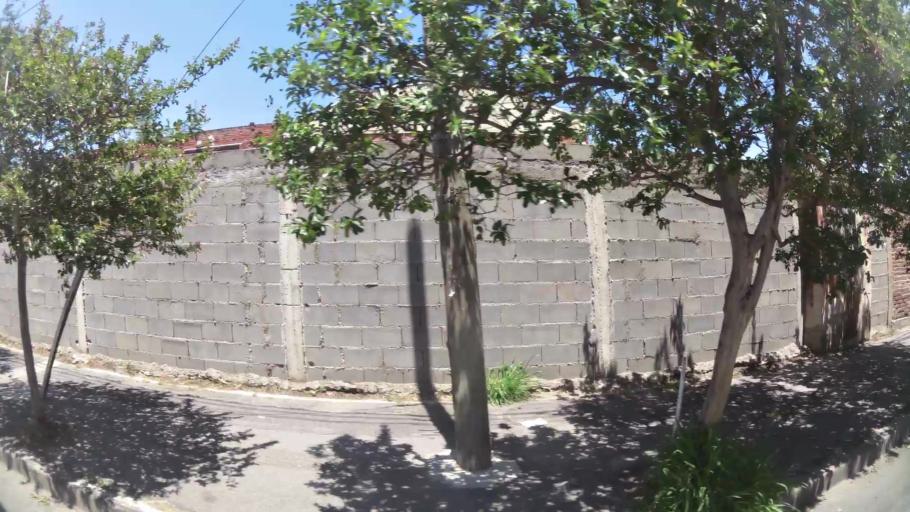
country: AR
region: Cordoba
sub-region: Departamento de Capital
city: Cordoba
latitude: -31.3961
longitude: -64.2044
